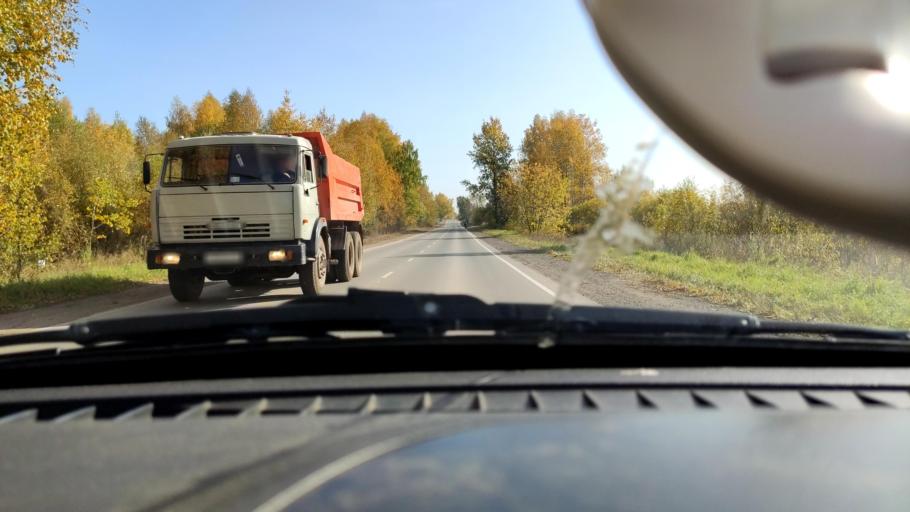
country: RU
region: Perm
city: Overyata
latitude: 58.0571
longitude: 55.8566
